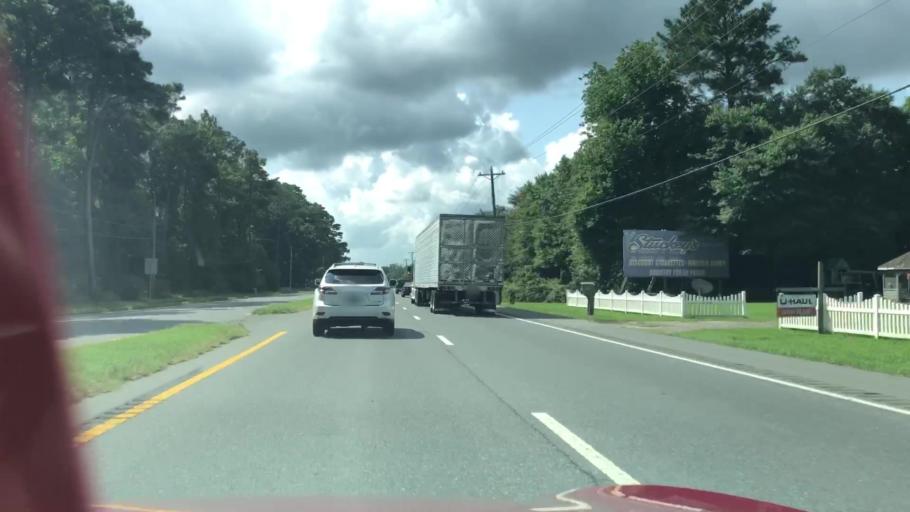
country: US
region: Virginia
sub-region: Accomack County
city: Wattsville
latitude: 37.8996
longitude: -75.5490
